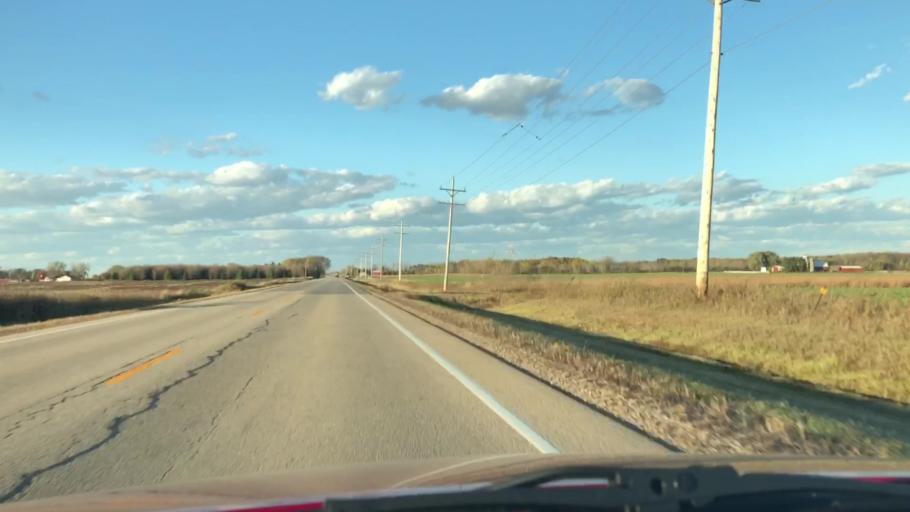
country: US
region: Wisconsin
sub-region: Outagamie County
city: Seymour
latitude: 44.4653
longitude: -88.2911
